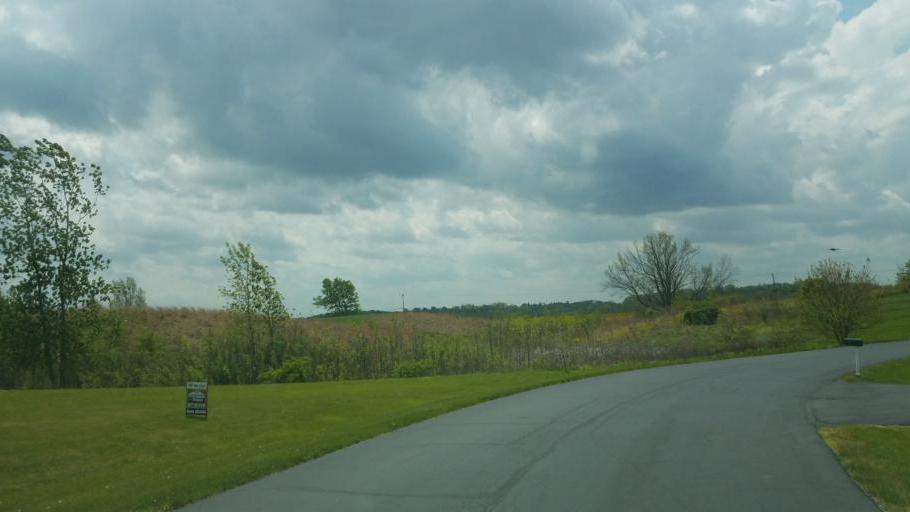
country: US
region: Ohio
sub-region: Perry County
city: Thornport
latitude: 39.9180
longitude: -82.4224
